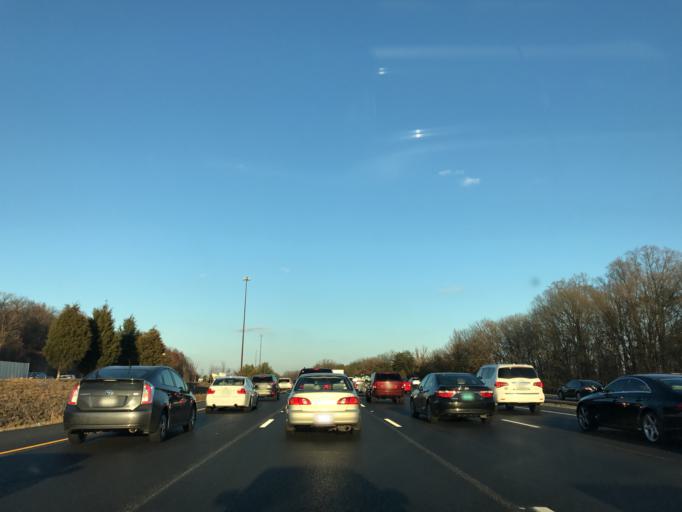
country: US
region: Maryland
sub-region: Prince George's County
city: West Laurel
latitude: 39.1066
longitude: -76.8839
